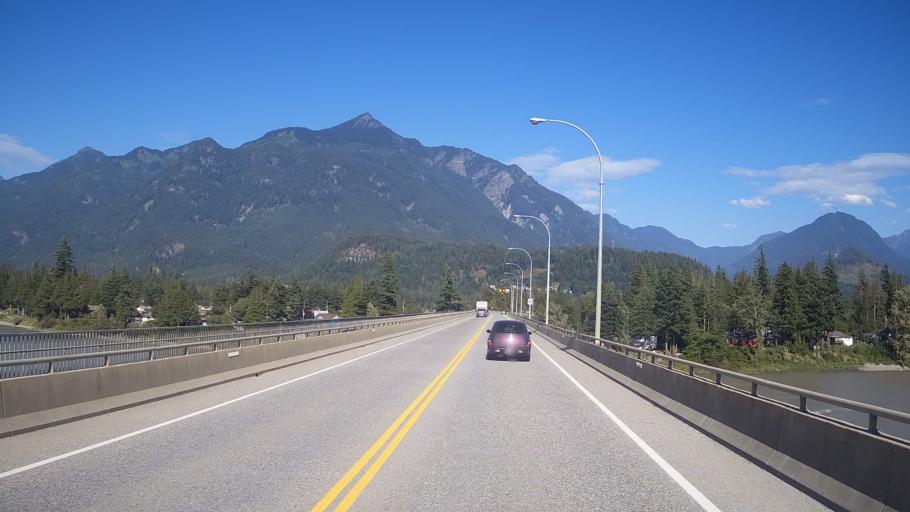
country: CA
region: British Columbia
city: Hope
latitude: 49.3860
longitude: -121.4543
